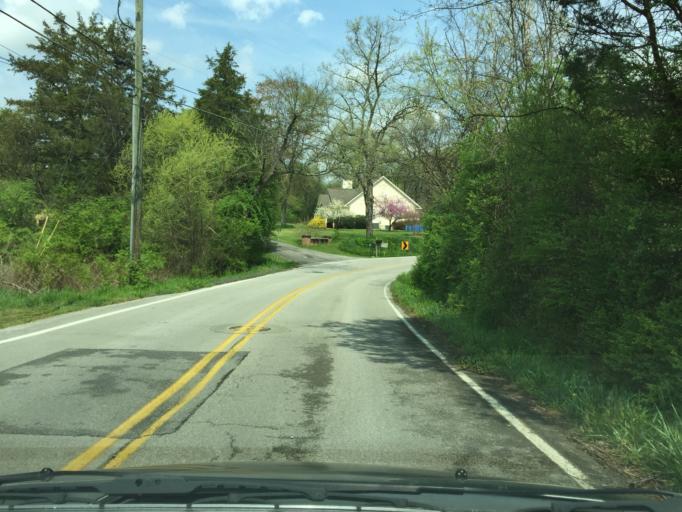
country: US
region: Tennessee
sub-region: Hamilton County
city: Walden
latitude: 35.1516
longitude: -85.2840
